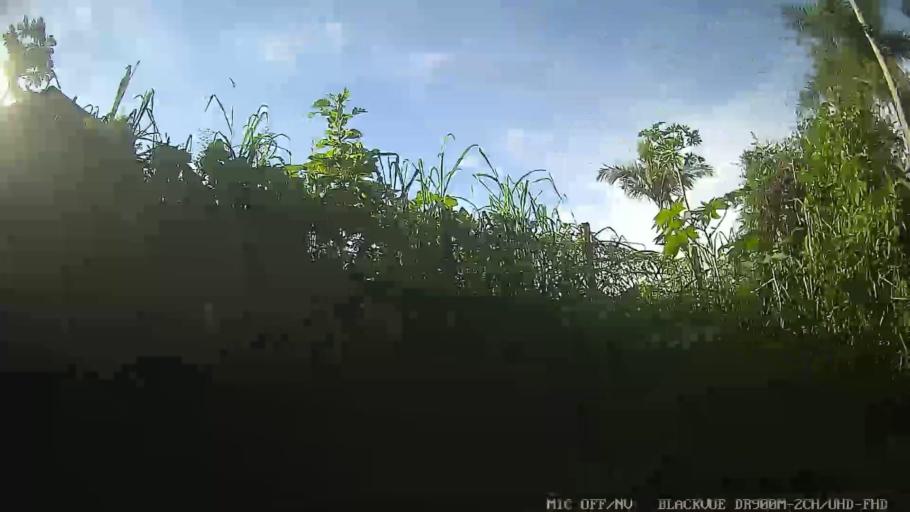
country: BR
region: Sao Paulo
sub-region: Tiete
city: Tiete
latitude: -23.0862
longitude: -47.6942
